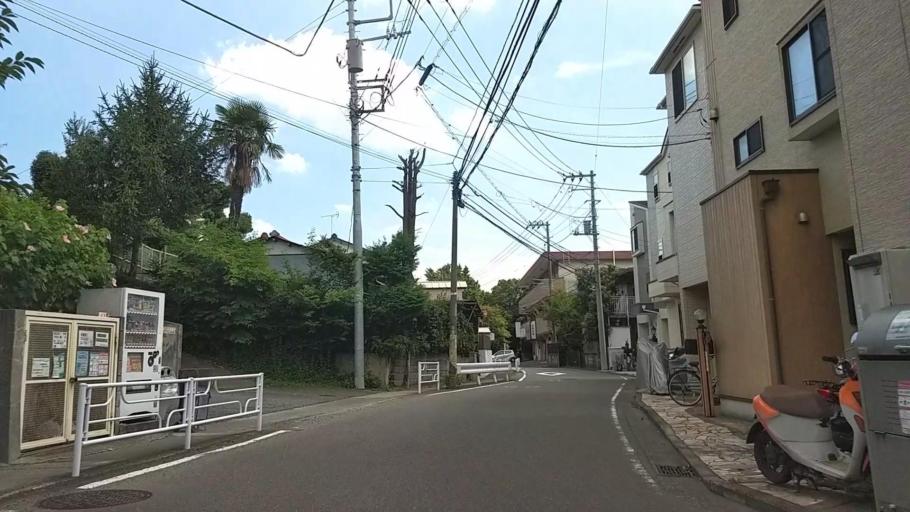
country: JP
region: Kanagawa
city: Yokohama
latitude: 35.5221
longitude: 139.5762
